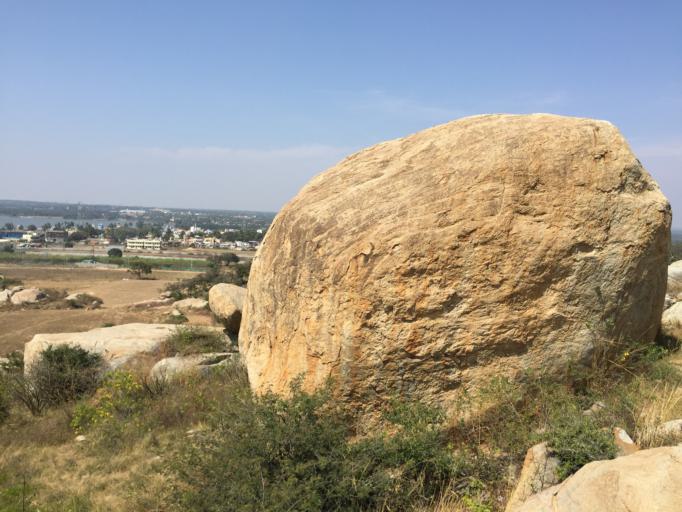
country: IN
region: Karnataka
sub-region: Kolar
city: Kolar
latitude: 13.1380
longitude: 78.0135
